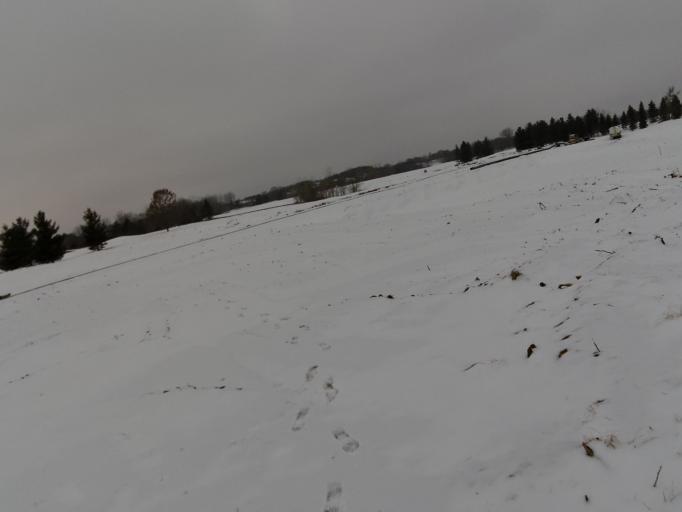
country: US
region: Minnesota
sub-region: Washington County
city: Lake Elmo
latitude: 44.9671
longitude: -92.8694
